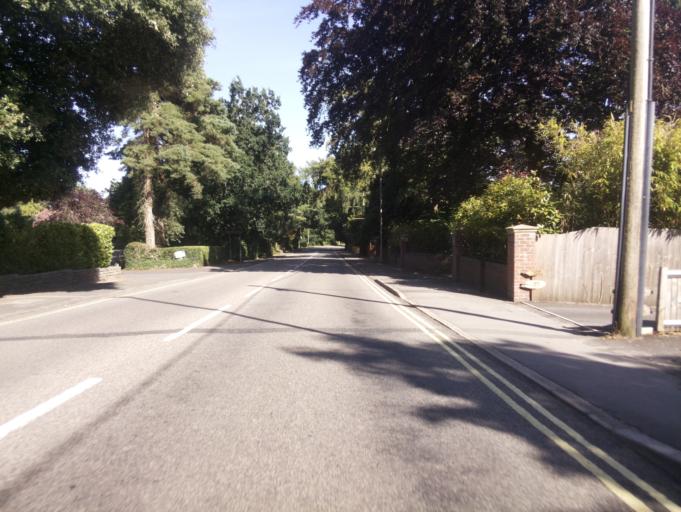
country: GB
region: England
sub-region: Dorset
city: Ferndown
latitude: 50.8002
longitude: -1.8881
